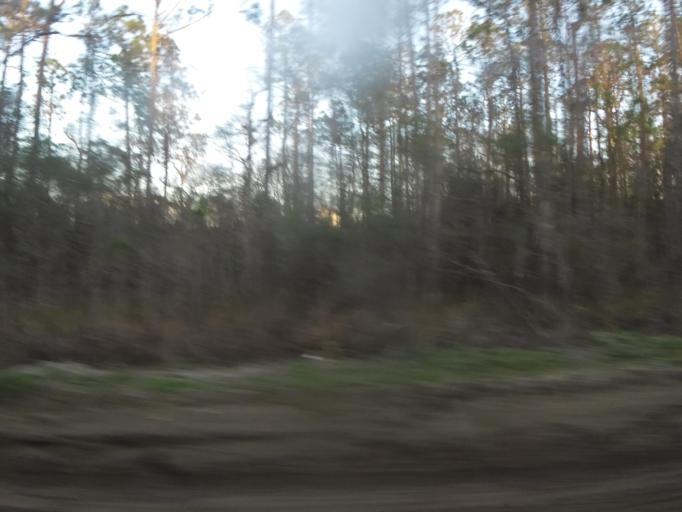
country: US
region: Florida
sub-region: Clay County
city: Green Cove Springs
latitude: 29.8470
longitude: -81.7969
